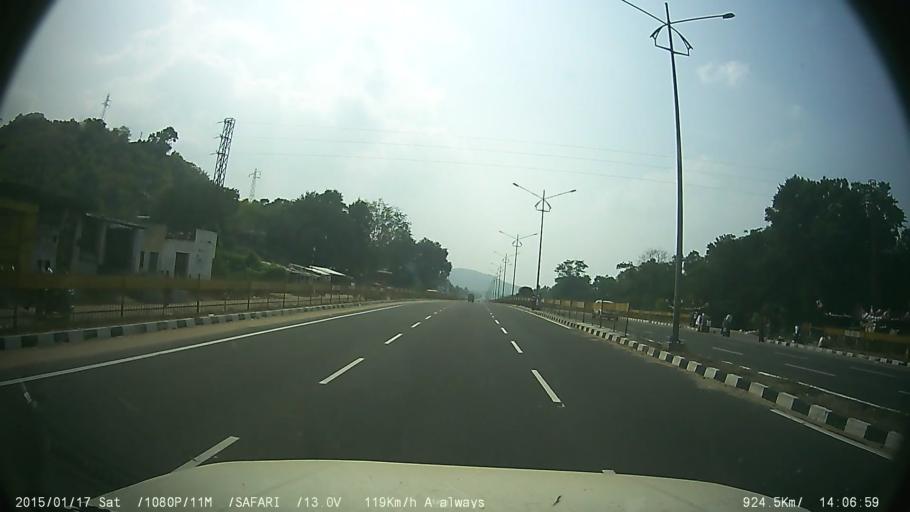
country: IN
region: Tamil Nadu
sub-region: Vellore
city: Ambur
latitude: 12.8341
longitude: 78.7836
